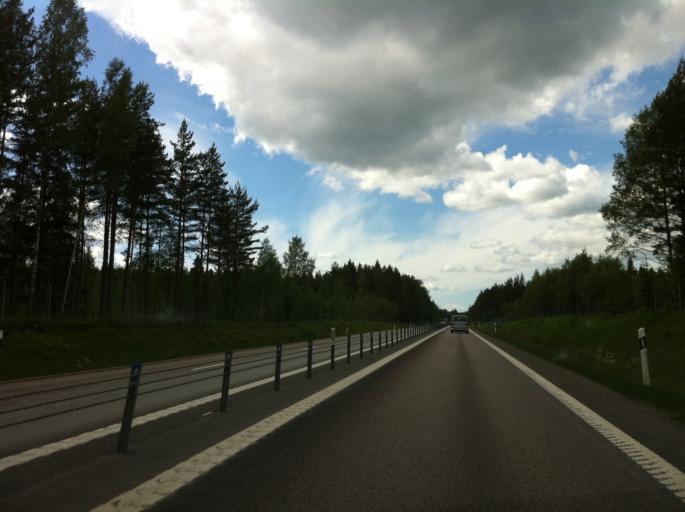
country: SE
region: Vaestra Goetaland
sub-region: Amals Kommun
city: Amal
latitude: 59.1077
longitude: 12.8002
